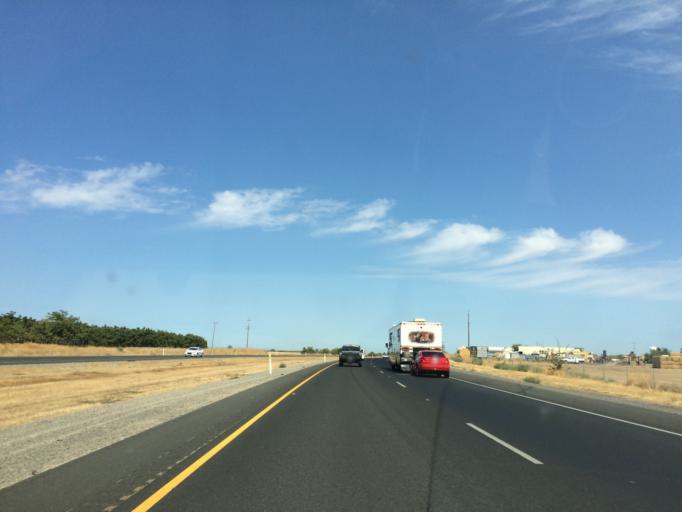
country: US
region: California
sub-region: Colusa County
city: Arbuckle
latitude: 38.9675
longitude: -122.0267
